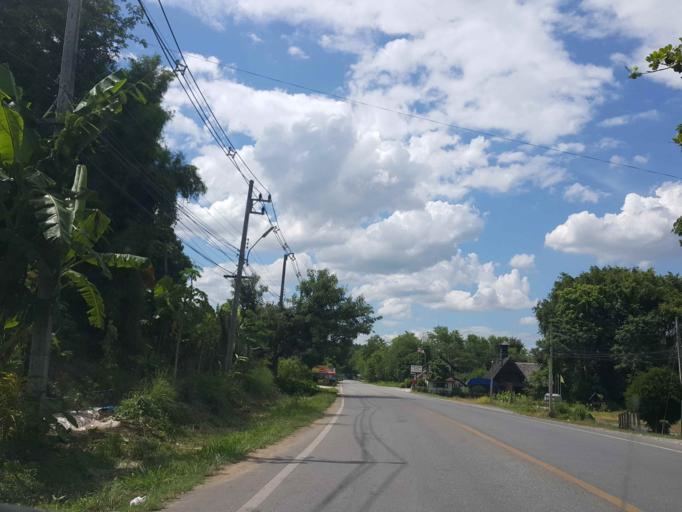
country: TH
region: Chiang Mai
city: Chiang Mai
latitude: 18.9104
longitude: 98.9060
